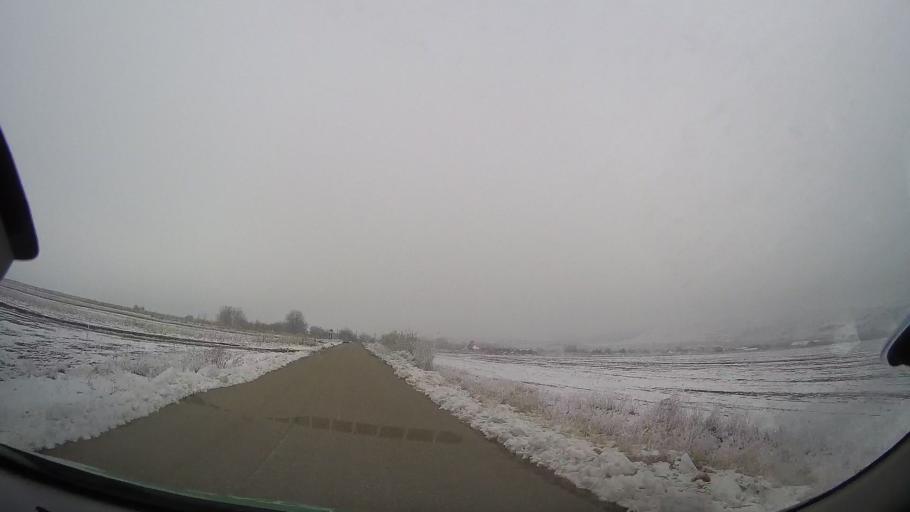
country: RO
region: Vaslui
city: Coroiesti
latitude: 46.2401
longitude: 27.4789
